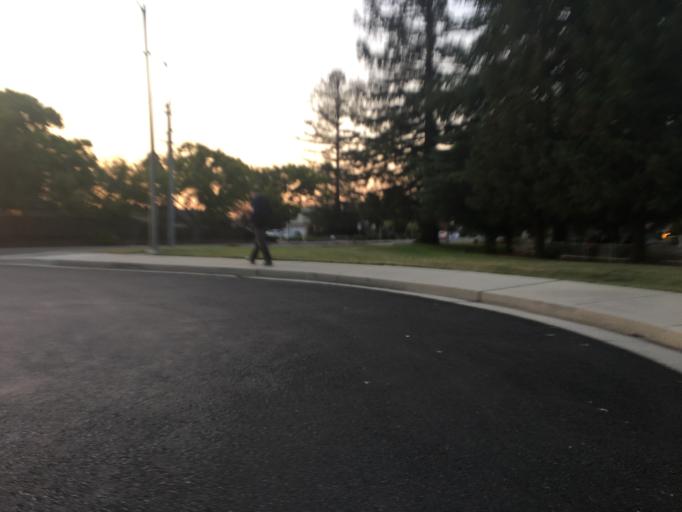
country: US
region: California
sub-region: Santa Clara County
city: Cupertino
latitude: 37.3106
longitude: -122.0410
